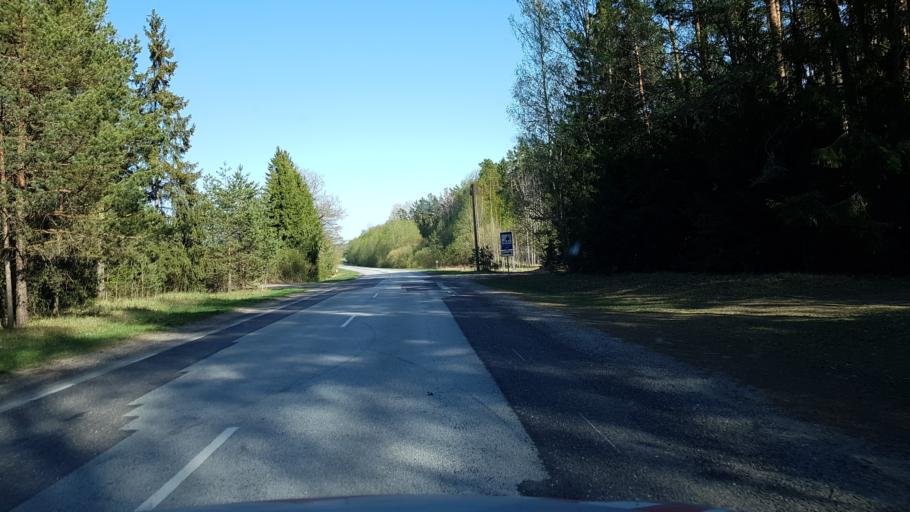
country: EE
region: Paernumaa
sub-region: Paikuse vald
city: Paikuse
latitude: 58.3446
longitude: 24.6776
